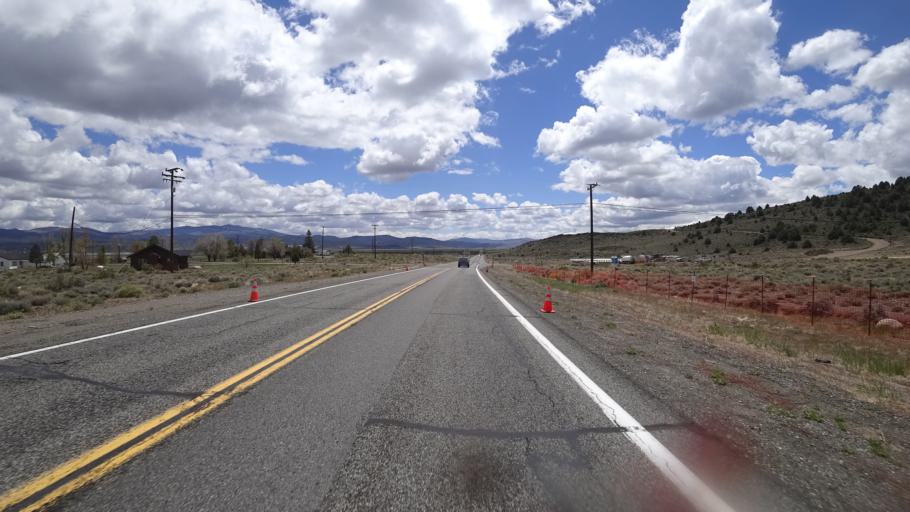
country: US
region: California
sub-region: Mono County
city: Bridgeport
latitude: 38.2770
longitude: -119.2899
